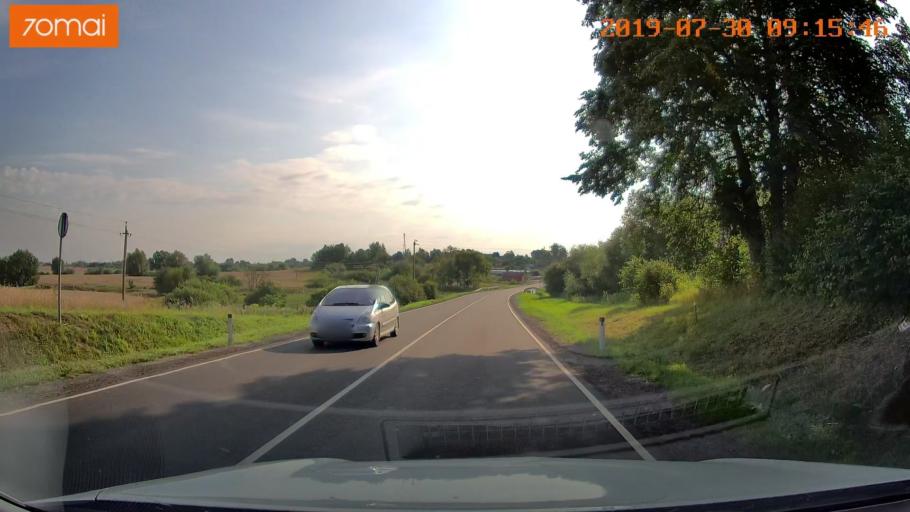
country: RU
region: Kaliningrad
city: Nesterov
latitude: 54.6334
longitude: 22.5466
